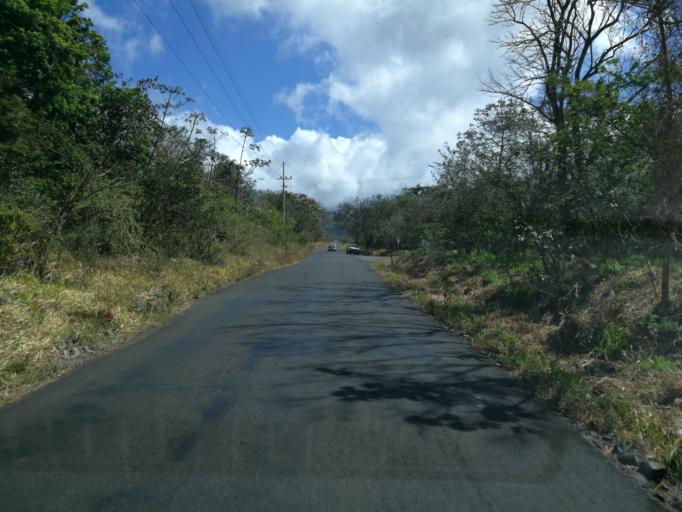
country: CR
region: Guanacaste
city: Liberia
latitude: 10.7555
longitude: -85.3657
